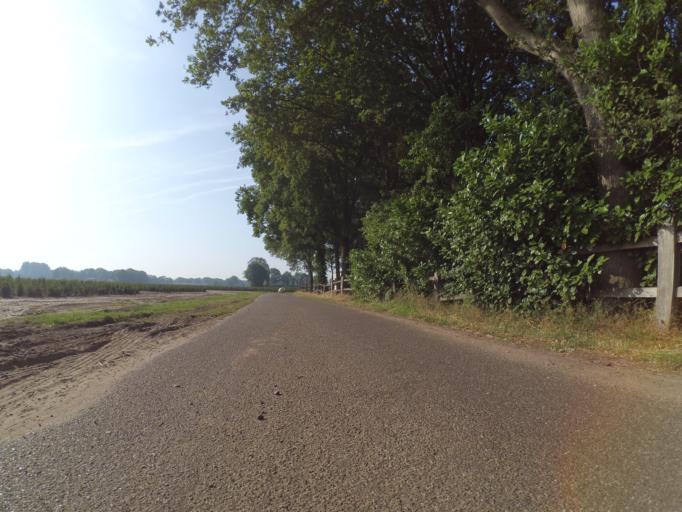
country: NL
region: Overijssel
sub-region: Gemeente Borne
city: Borne
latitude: 52.3430
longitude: 6.7942
